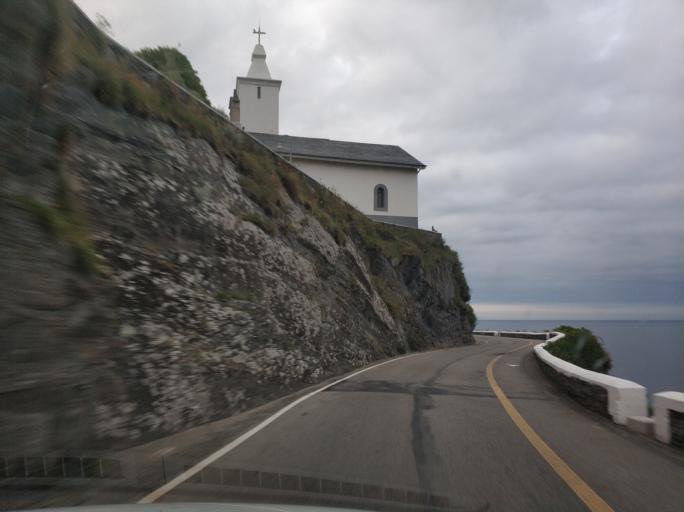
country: ES
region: Asturias
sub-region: Province of Asturias
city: Navia
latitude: 43.5490
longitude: -6.5322
